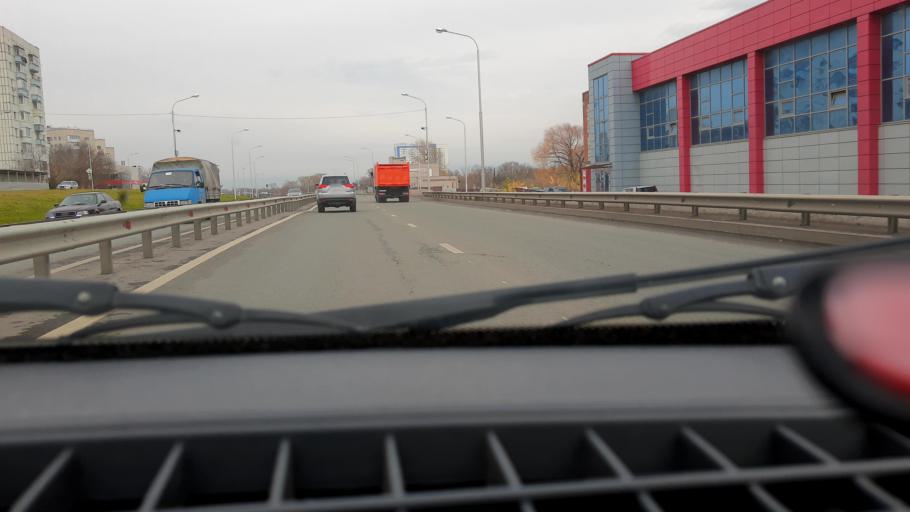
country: RU
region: Bashkortostan
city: Ufa
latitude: 54.7998
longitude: 56.1228
